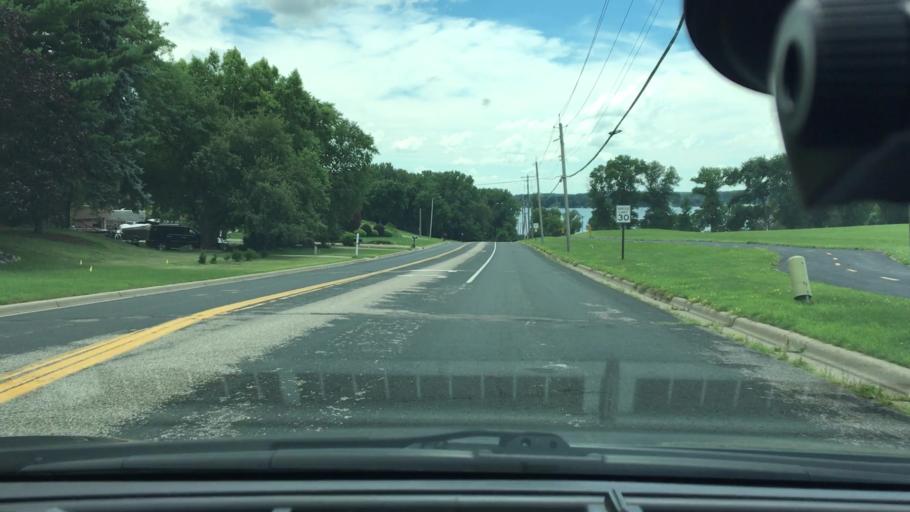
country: US
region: Minnesota
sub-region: Hennepin County
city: Plymouth
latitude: 45.0213
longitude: -93.4209
